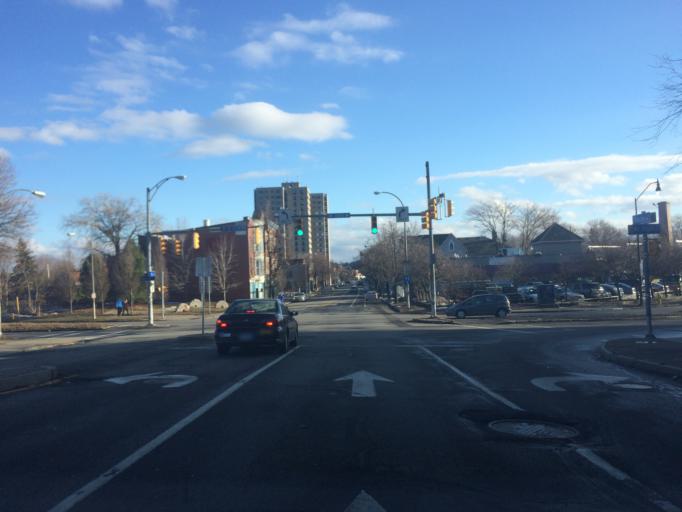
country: US
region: New York
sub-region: Monroe County
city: Rochester
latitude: 43.1491
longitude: -77.6064
